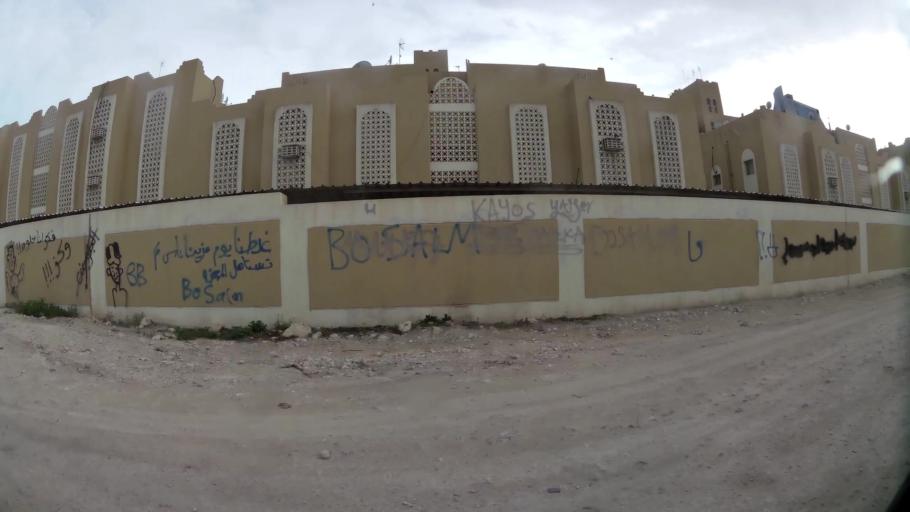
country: QA
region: Baladiyat ad Dawhah
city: Doha
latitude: 25.2886
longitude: 51.5087
